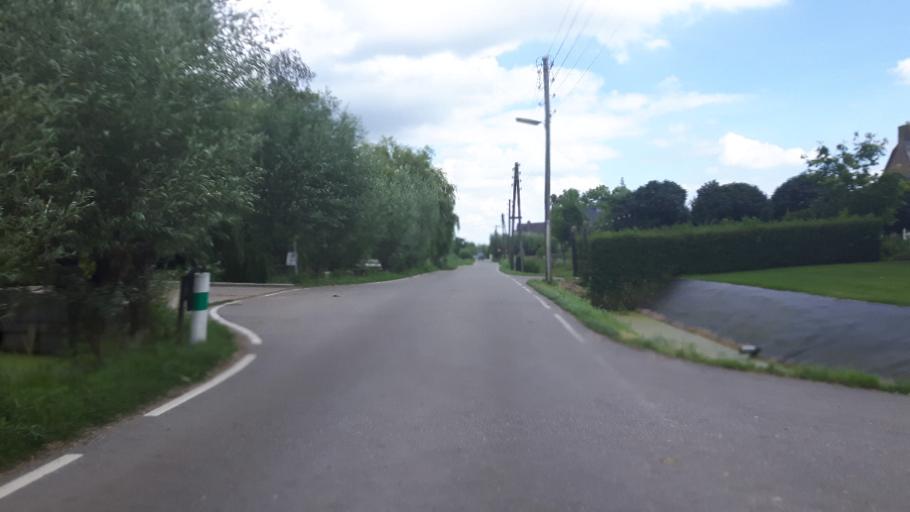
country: NL
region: South Holland
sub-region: Gemeente Vlist
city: Haastrecht
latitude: 51.9371
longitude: 4.7622
